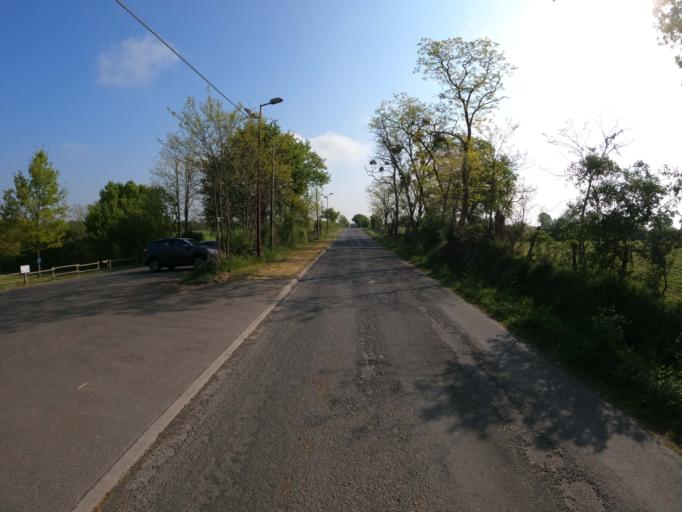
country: FR
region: Pays de la Loire
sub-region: Departement de Maine-et-Loire
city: Torfou
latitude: 47.0423
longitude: -1.1103
